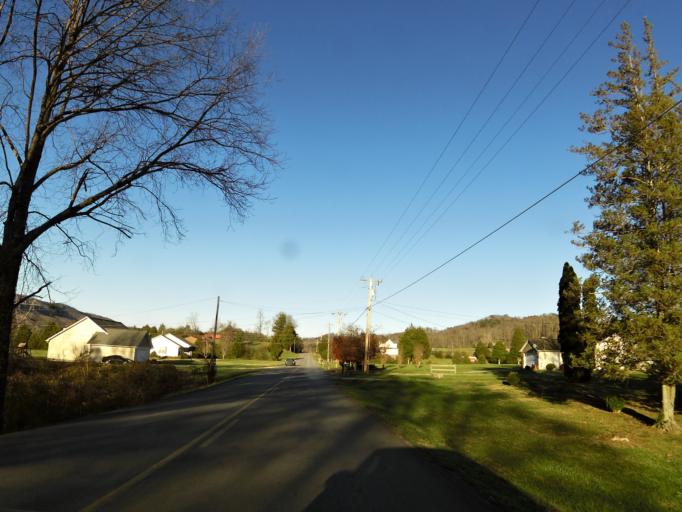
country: US
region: Tennessee
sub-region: Anderson County
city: Clinton
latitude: 36.1477
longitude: -84.1786
